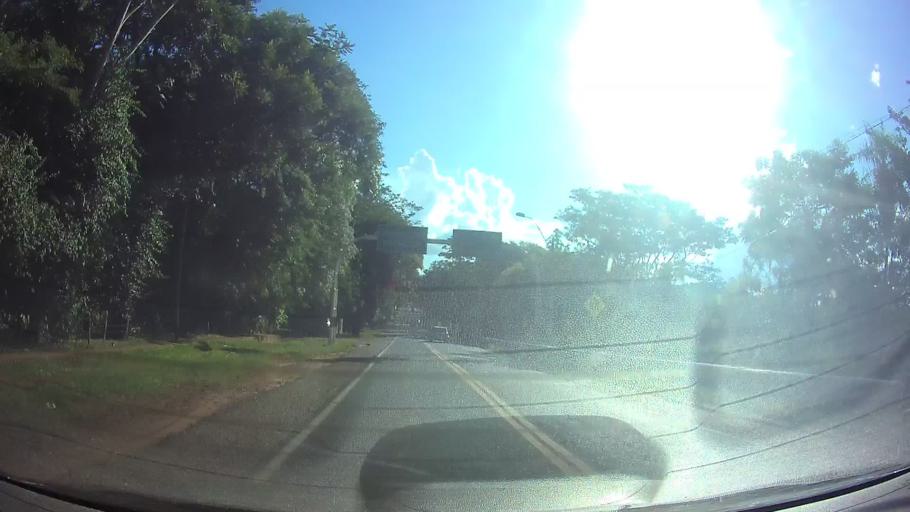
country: PY
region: Central
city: Aregua
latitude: -25.3207
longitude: -57.3893
